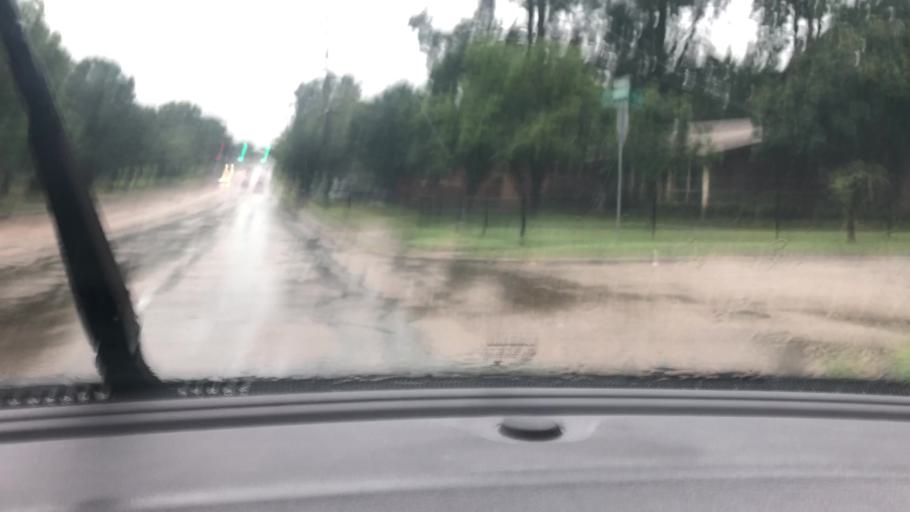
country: US
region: Texas
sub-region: Bowie County
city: Wake Village
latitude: 33.4475
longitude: -94.0805
